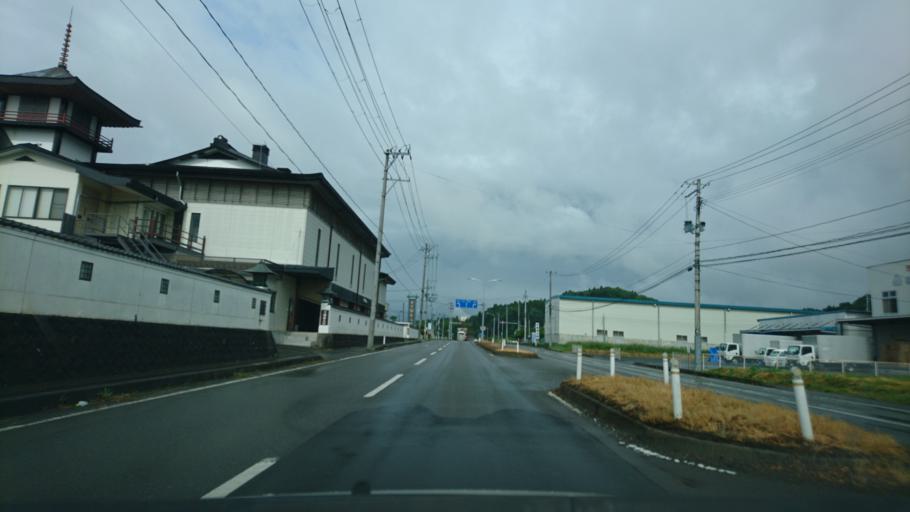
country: JP
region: Iwate
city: Ichinoseki
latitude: 38.9408
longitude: 141.0848
